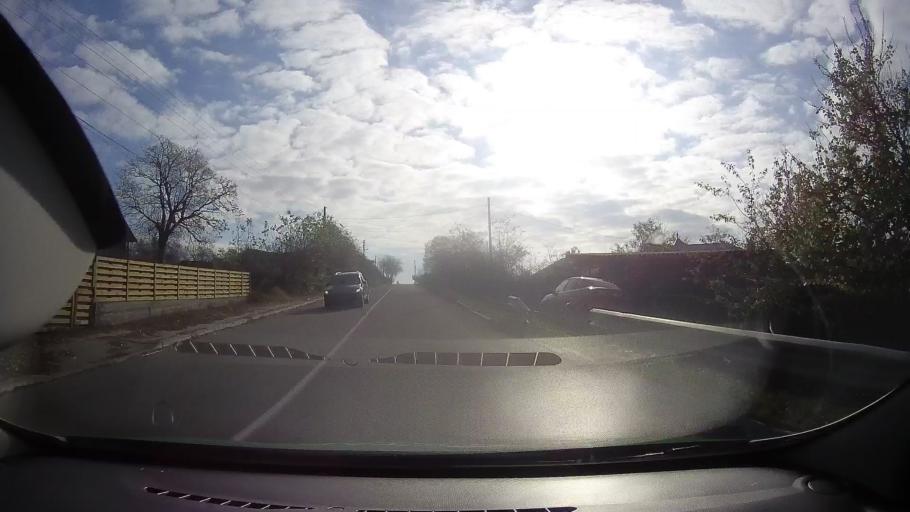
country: RO
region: Tulcea
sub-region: Comuna Bestepe
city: Bestepe
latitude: 45.0855
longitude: 29.0194
